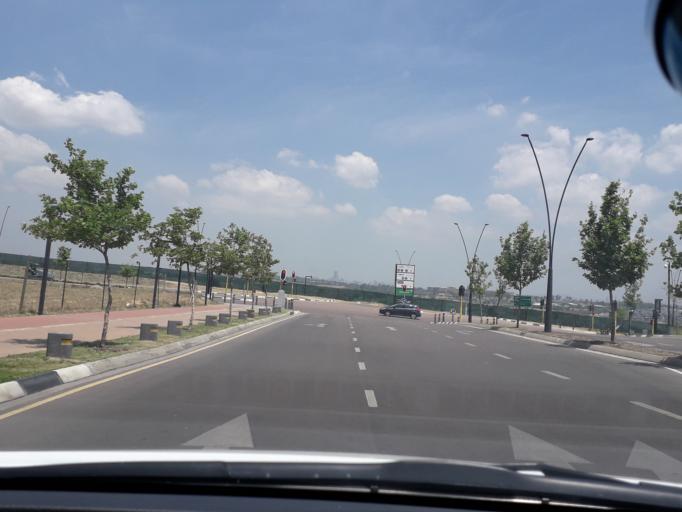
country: ZA
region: Gauteng
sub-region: City of Johannesburg Metropolitan Municipality
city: Midrand
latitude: -26.0155
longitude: 28.1040
